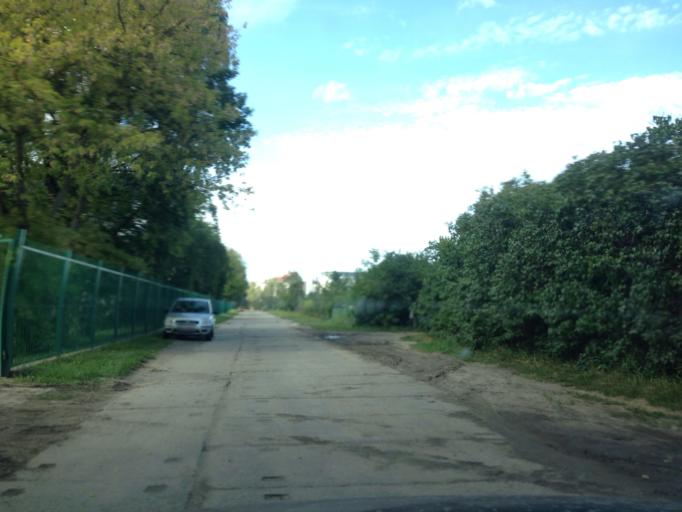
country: PL
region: Pomeranian Voivodeship
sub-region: Gdansk
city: Gdansk
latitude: 54.3983
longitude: 18.6165
